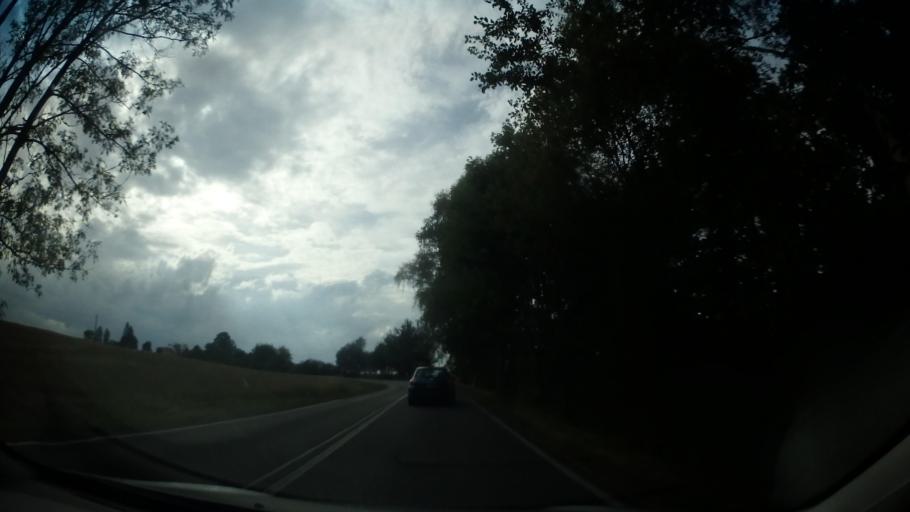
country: CZ
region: Pardubicky
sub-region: Okres Chrudim
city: Sec
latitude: 49.8509
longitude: 15.6734
